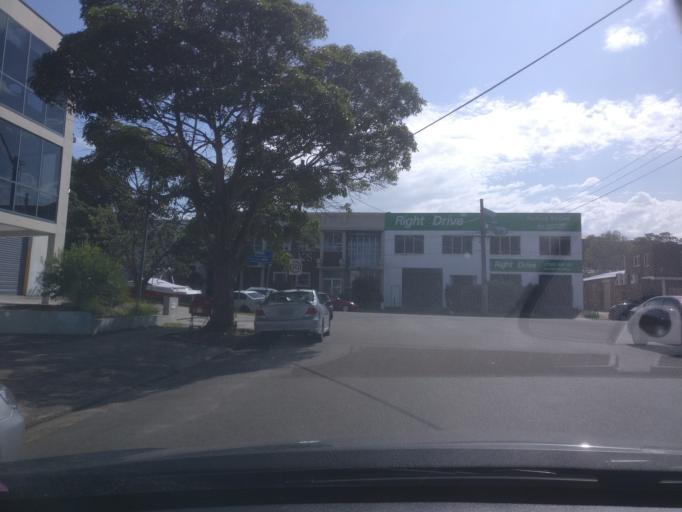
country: AU
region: New South Wales
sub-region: Warringah
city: Brookvale
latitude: -33.7646
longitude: 151.2654
